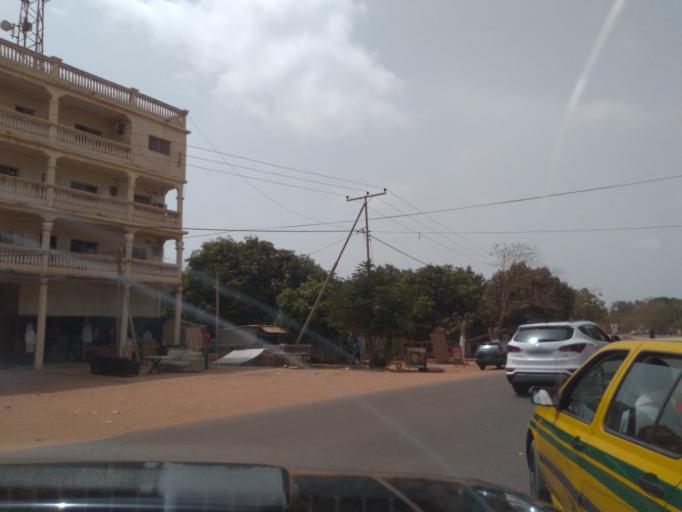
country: GM
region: Western
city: Sukuta
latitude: 13.4413
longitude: -16.7033
